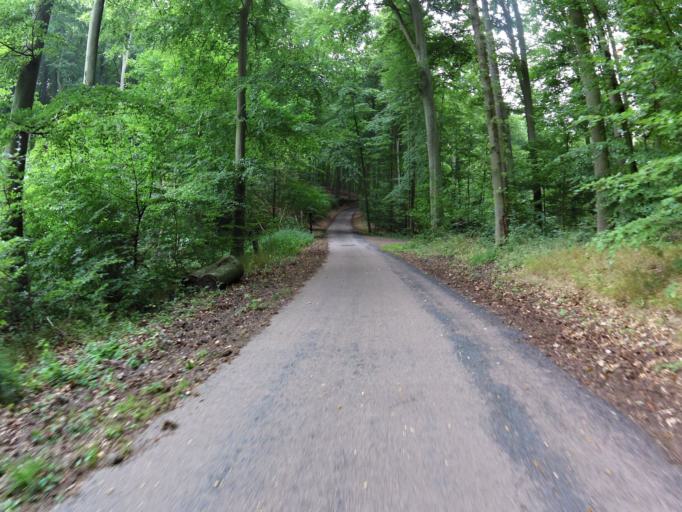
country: DE
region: Mecklenburg-Vorpommern
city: Seebad Heringsdorf
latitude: 53.9048
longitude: 14.1622
